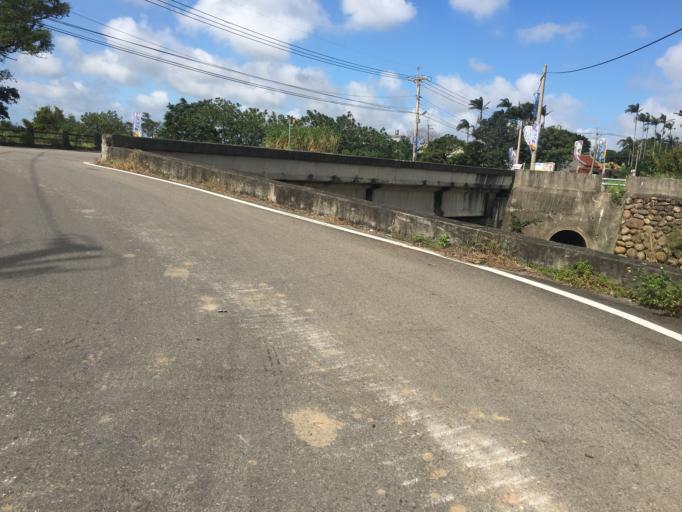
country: TW
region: Taiwan
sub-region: Hsinchu
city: Zhubei
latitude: 24.8843
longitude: 121.0454
